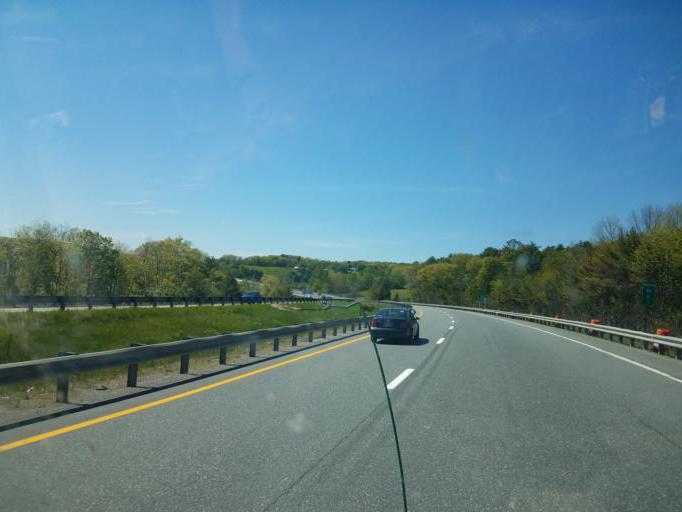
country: US
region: New Hampshire
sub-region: Grafton County
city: Lebanon
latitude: 43.6387
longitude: -72.2141
